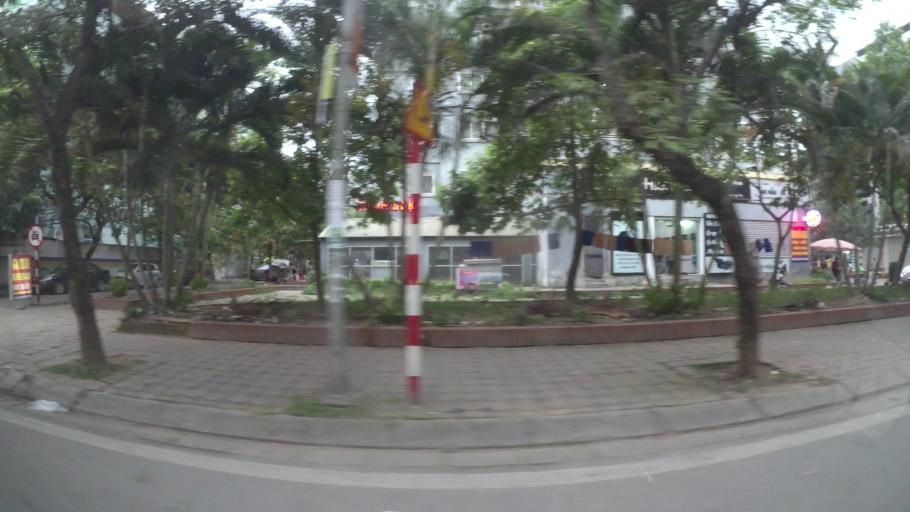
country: VN
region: Ha Noi
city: Cau Dien
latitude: 21.0360
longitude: 105.7646
